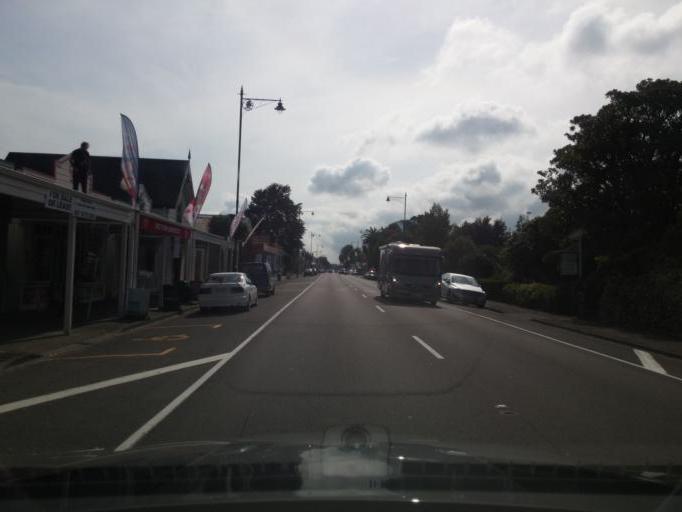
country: NZ
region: Wellington
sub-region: Masterton District
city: Masterton
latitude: -41.0823
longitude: 175.4582
